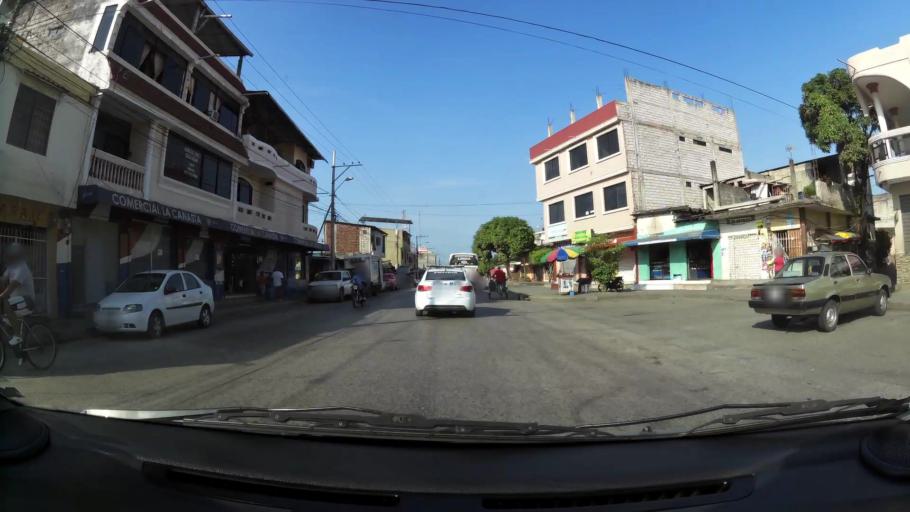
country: EC
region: Guayas
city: Eloy Alfaro
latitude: -2.1780
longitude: -79.8442
